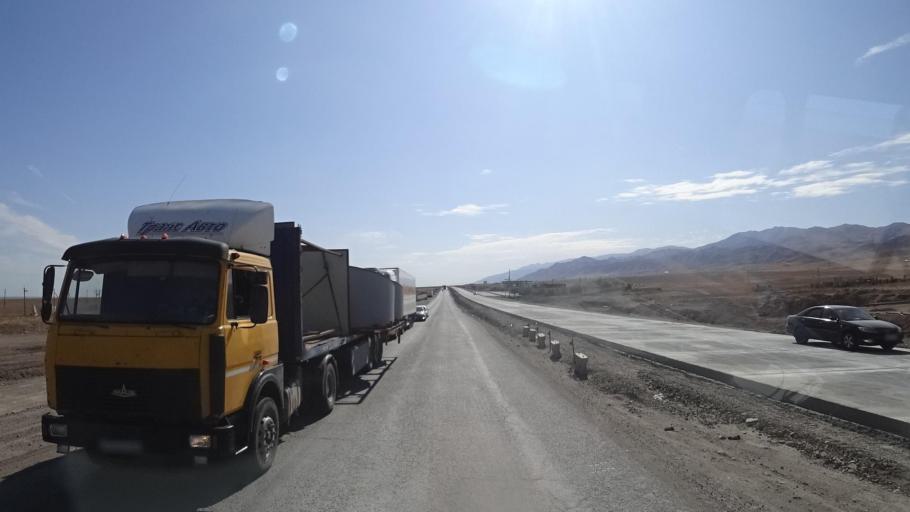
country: KG
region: Chuy
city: Ivanovka
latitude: 43.4014
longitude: 75.1111
